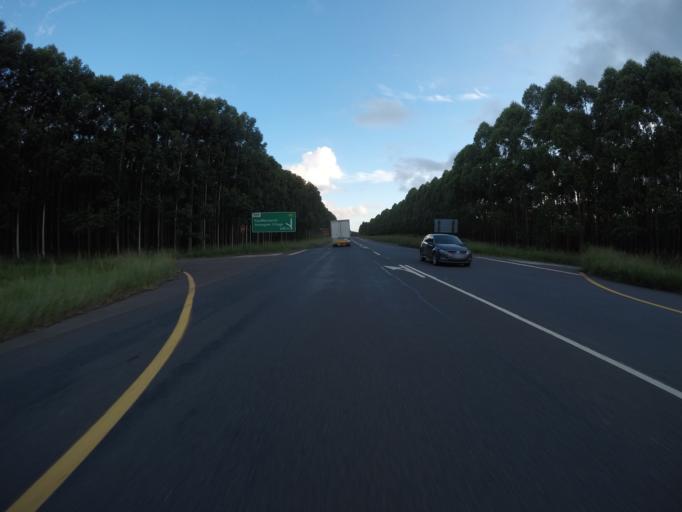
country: ZA
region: KwaZulu-Natal
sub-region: uThungulu District Municipality
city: KwaMbonambi
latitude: -28.5868
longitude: 32.0993
